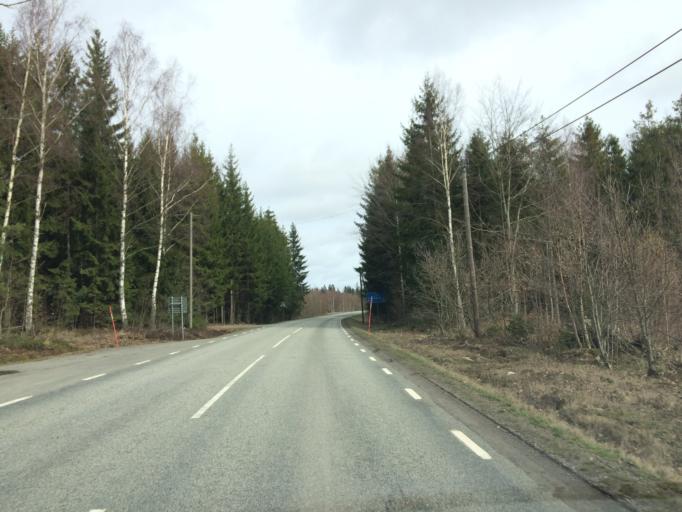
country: SE
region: Skane
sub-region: Osby Kommun
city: Lonsboda
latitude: 56.4037
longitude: 14.3304
